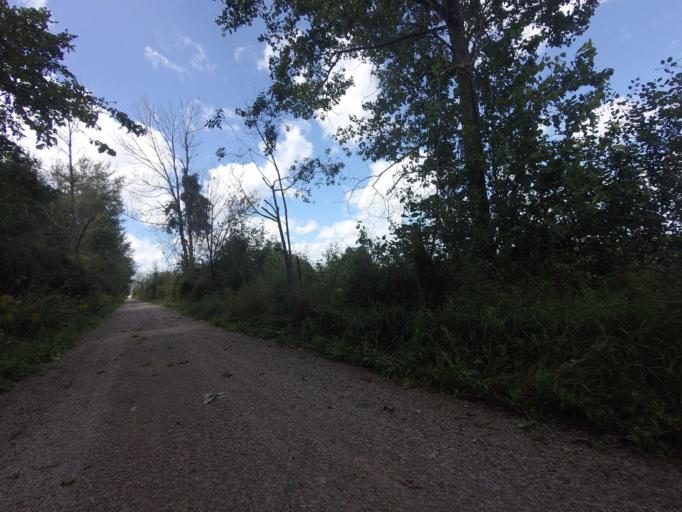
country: CA
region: Ontario
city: Huron East
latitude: 43.6387
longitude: -81.1986
